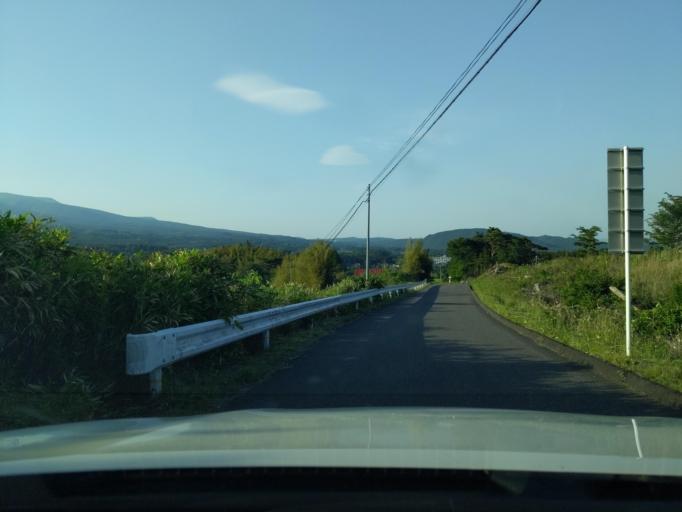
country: JP
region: Fukushima
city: Motomiya
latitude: 37.5305
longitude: 140.3344
